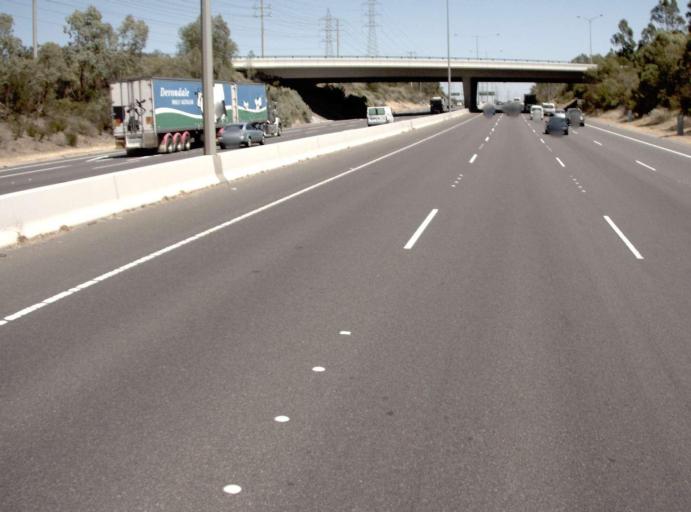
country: AU
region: Victoria
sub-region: Hume
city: Campbellfield
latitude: -37.6910
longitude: 144.9691
